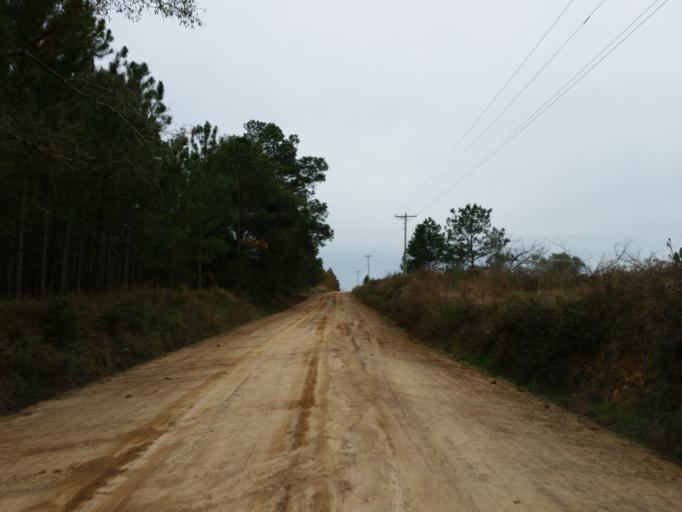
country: US
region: Georgia
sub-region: Crisp County
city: Cordele
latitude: 31.8632
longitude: -83.7337
